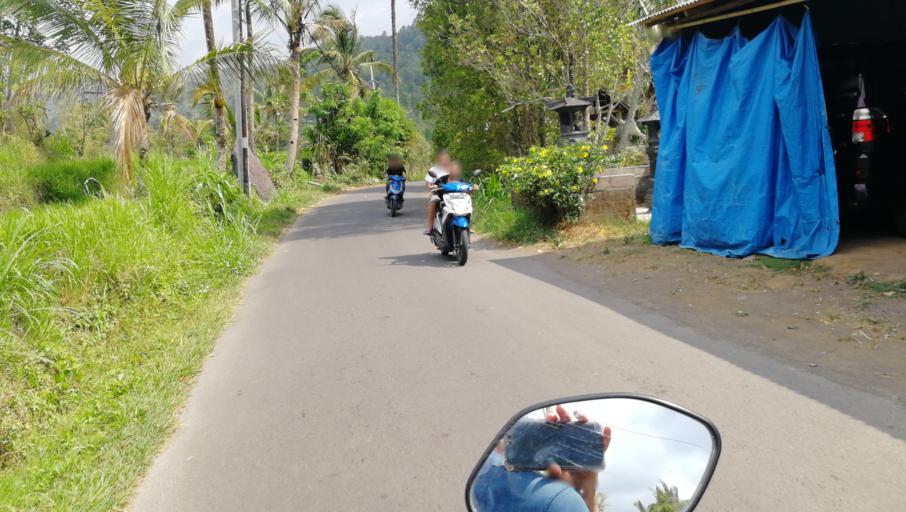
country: ID
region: Bali
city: Munduk
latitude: -8.2680
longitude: 115.0466
